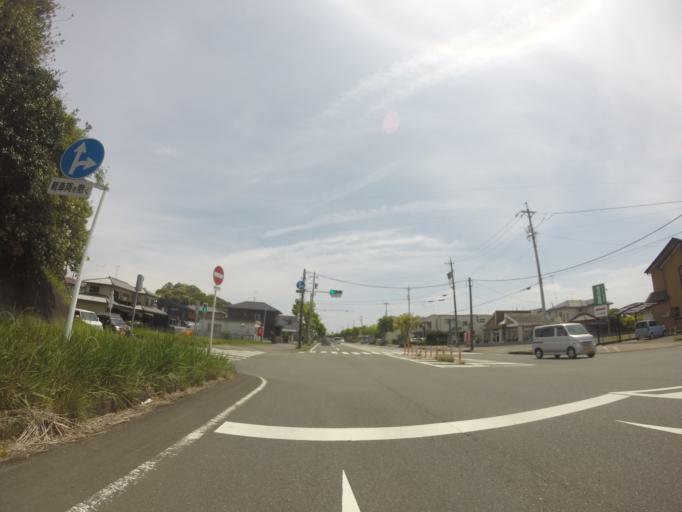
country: JP
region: Shizuoka
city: Fujieda
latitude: 34.8894
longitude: 138.2565
